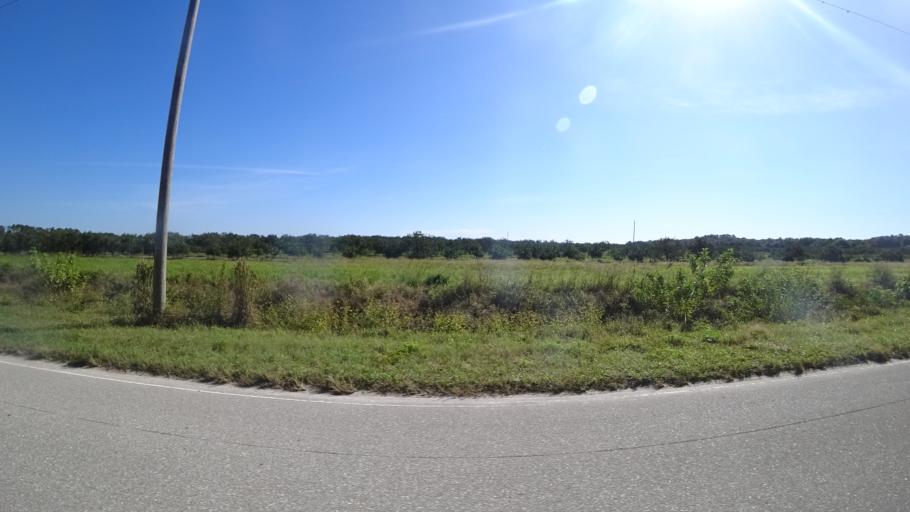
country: US
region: Florida
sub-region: Hillsborough County
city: Wimauma
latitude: 27.6228
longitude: -82.2926
